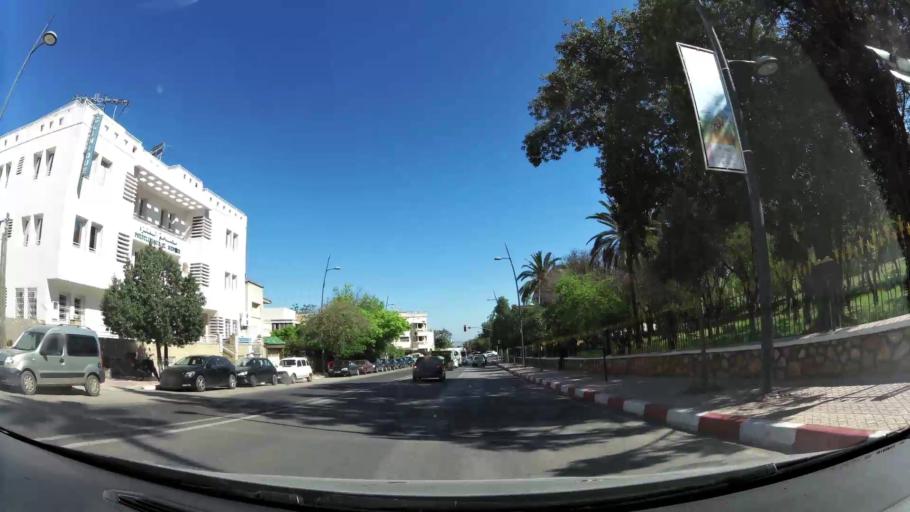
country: MA
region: Meknes-Tafilalet
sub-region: Meknes
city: Meknes
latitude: 33.9002
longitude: -5.5541
